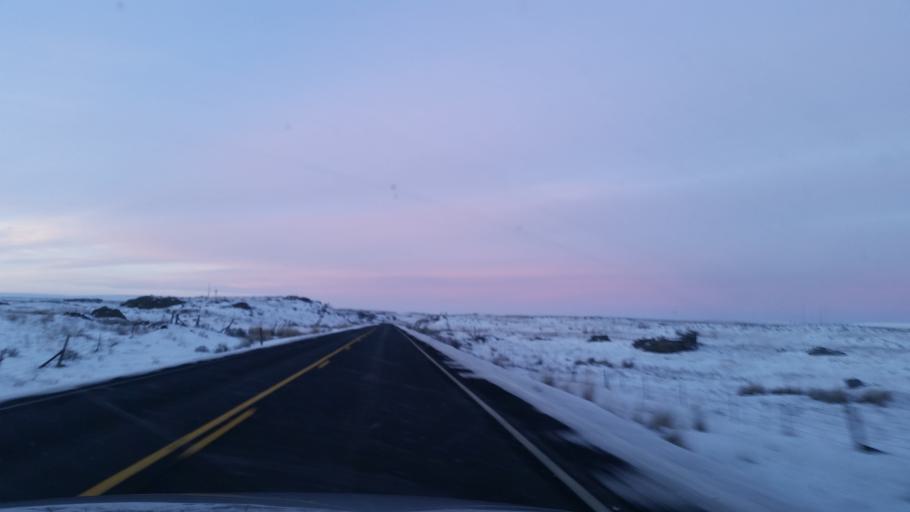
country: US
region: Washington
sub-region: Spokane County
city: Medical Lake
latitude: 47.2823
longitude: -117.9598
